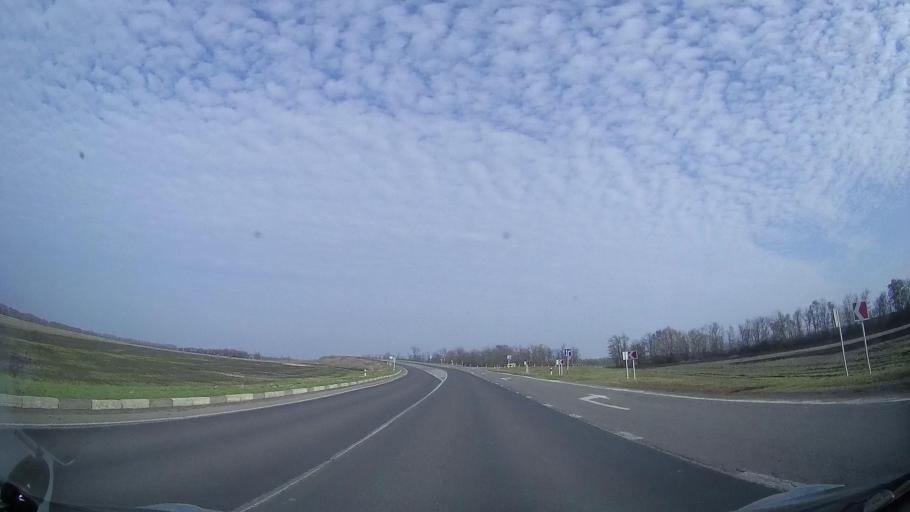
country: RU
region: Rostov
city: Tselina
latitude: 46.5245
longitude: 41.1646
